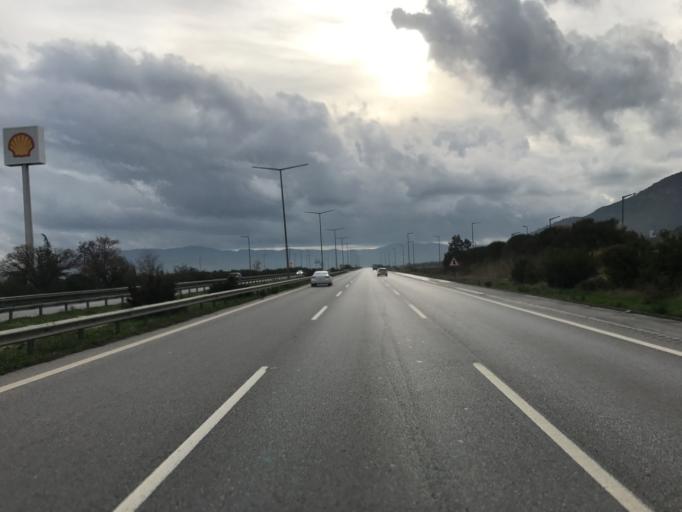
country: TR
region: Izmir
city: Belevi
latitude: 38.0698
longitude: 27.4114
